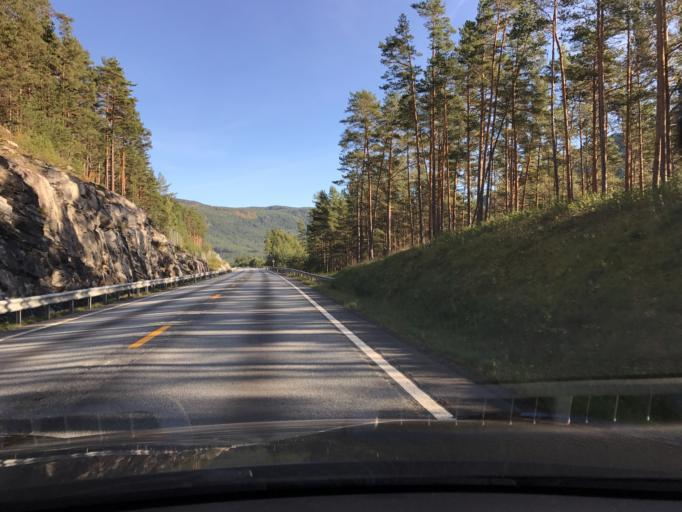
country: NO
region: Sogn og Fjordane
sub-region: Sogndal
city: Sogndalsfjora
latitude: 61.1844
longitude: 7.2600
